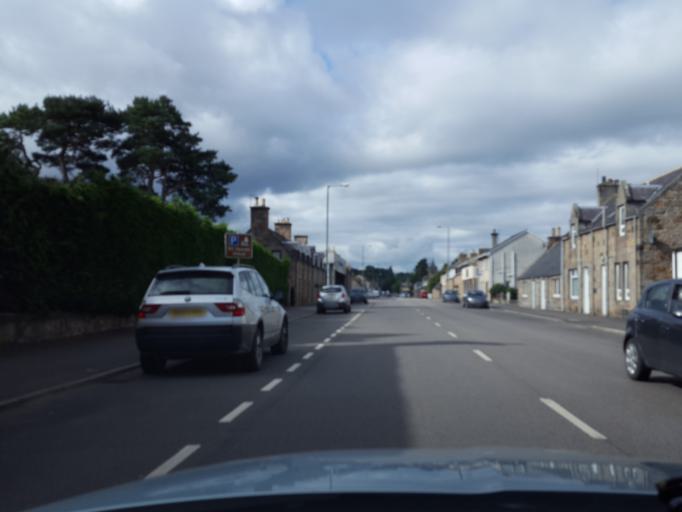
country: GB
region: Scotland
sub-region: Moray
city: Rothes
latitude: 57.4740
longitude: -3.2181
